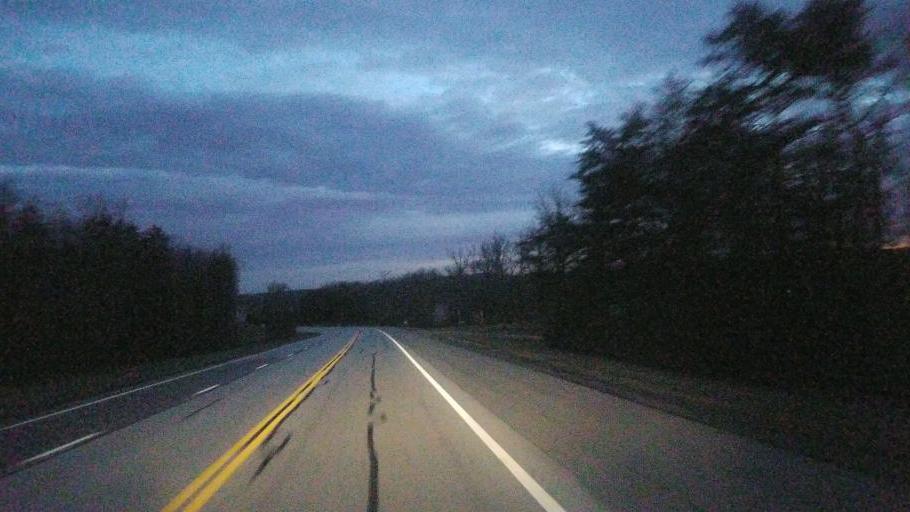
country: US
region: Tennessee
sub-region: Sequatchie County
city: Dunlap
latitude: 35.5172
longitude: -85.4710
